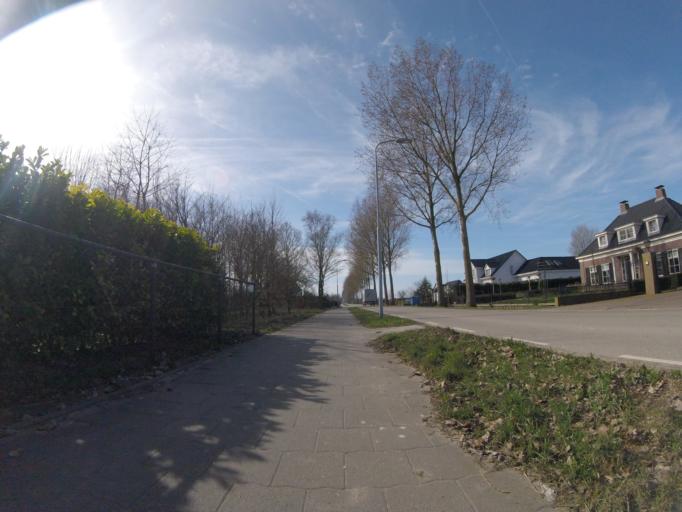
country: NL
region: North Holland
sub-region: Gemeente Bloemendaal
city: Bennebroek
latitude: 52.3179
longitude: 4.6312
